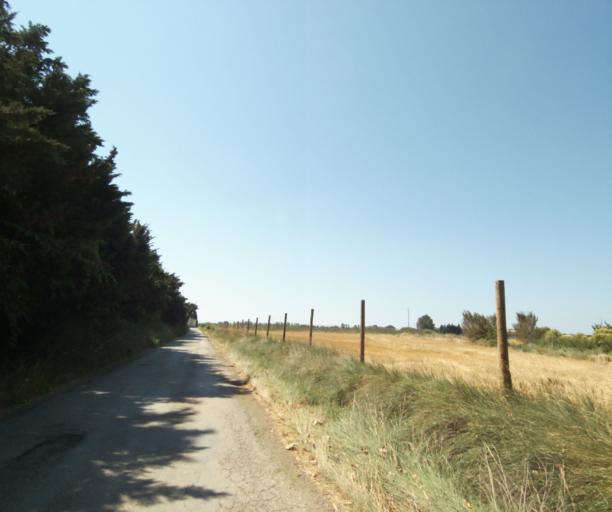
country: FR
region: Languedoc-Roussillon
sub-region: Departement de l'Herault
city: Marsillargues
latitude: 43.6510
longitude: 4.1661
